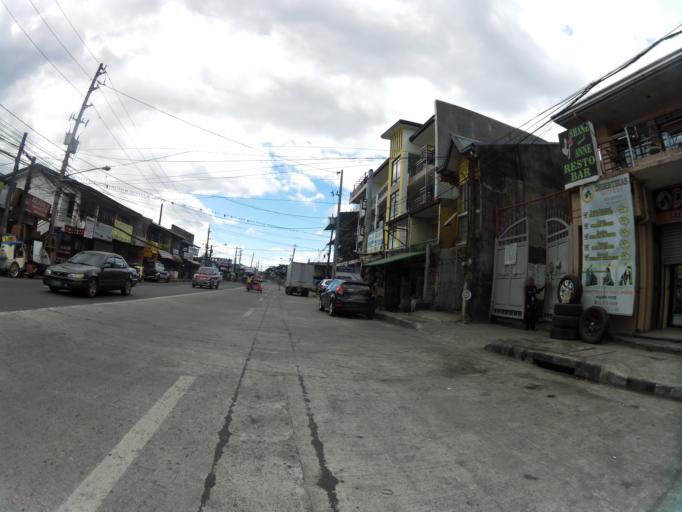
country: PH
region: Calabarzon
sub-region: Province of Rizal
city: Antipolo
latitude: 14.6299
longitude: 121.1199
